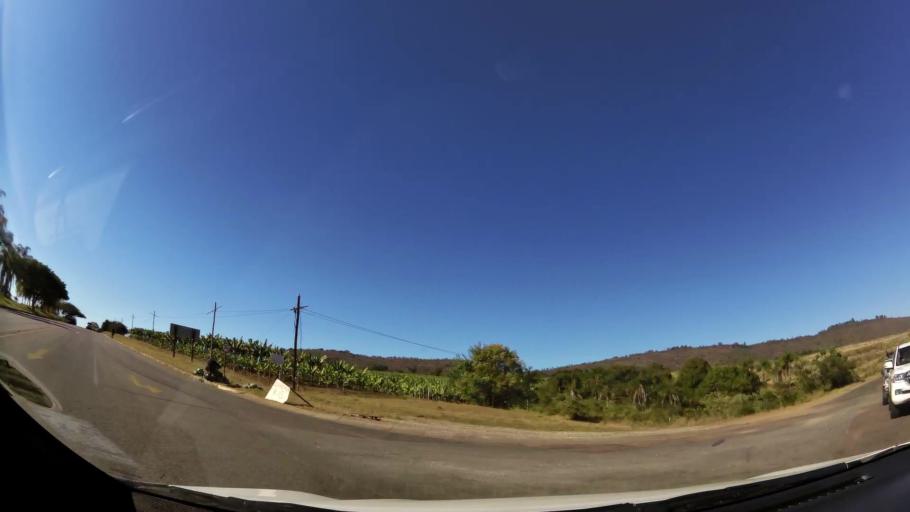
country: ZA
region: Limpopo
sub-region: Mopani District Municipality
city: Tzaneen
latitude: -23.8420
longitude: 30.1945
